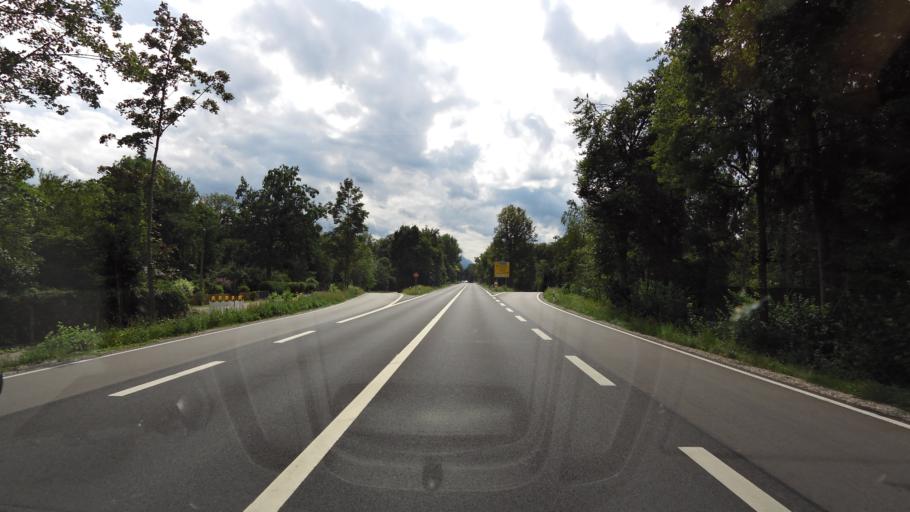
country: DE
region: Bavaria
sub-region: Upper Bavaria
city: Freilassing
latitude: 47.8258
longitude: 12.9751
